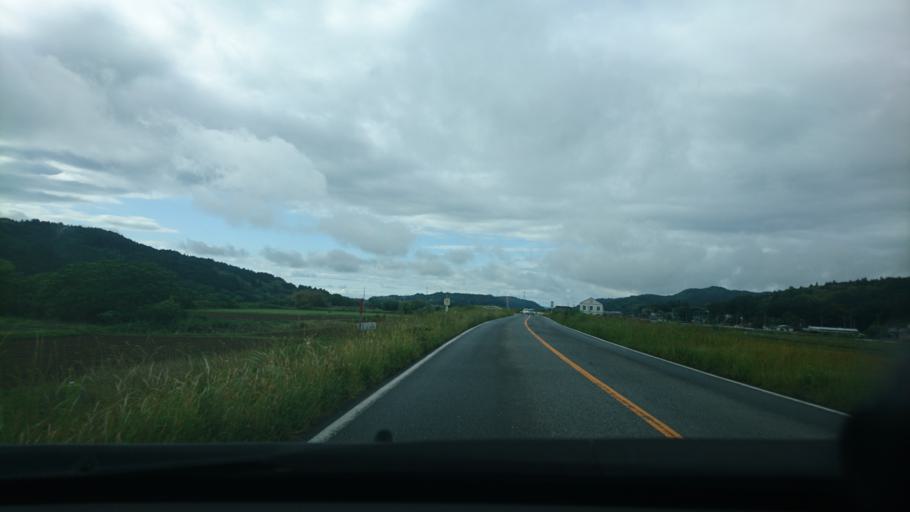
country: JP
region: Miyagi
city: Wakuya
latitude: 38.6370
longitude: 141.2888
